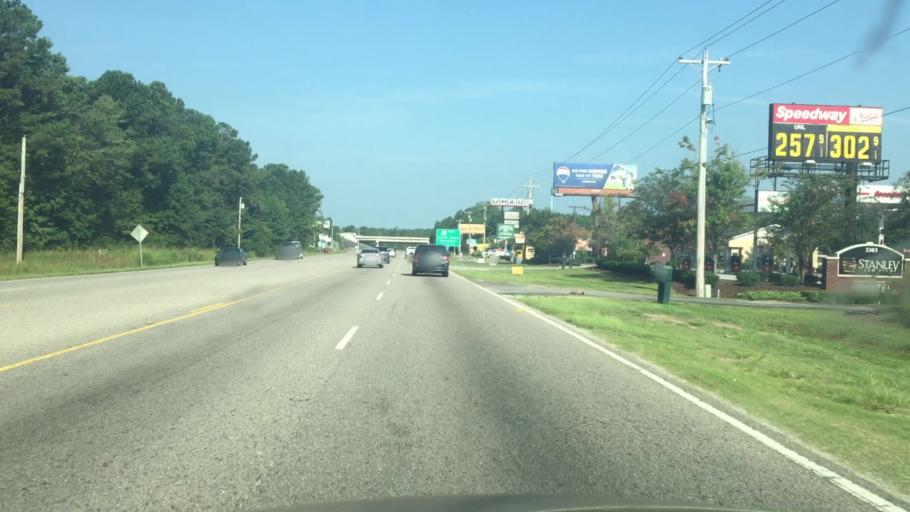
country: US
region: South Carolina
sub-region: Horry County
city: North Myrtle Beach
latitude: 33.8730
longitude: -78.6754
